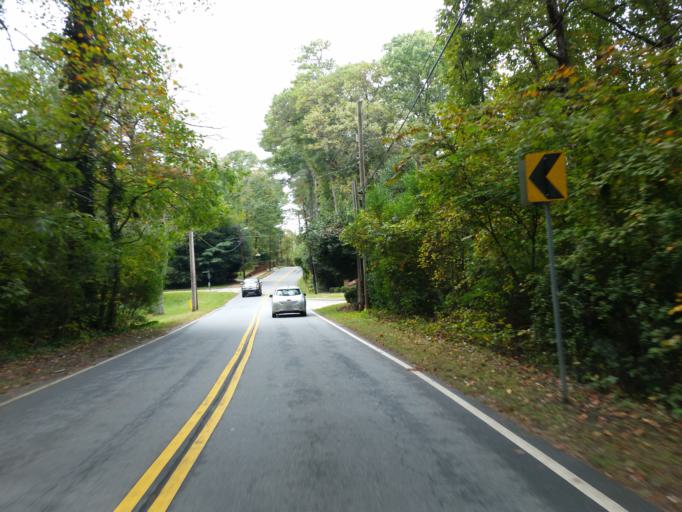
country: US
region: Georgia
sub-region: Fulton County
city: Sandy Springs
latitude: 33.9560
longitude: -84.3773
